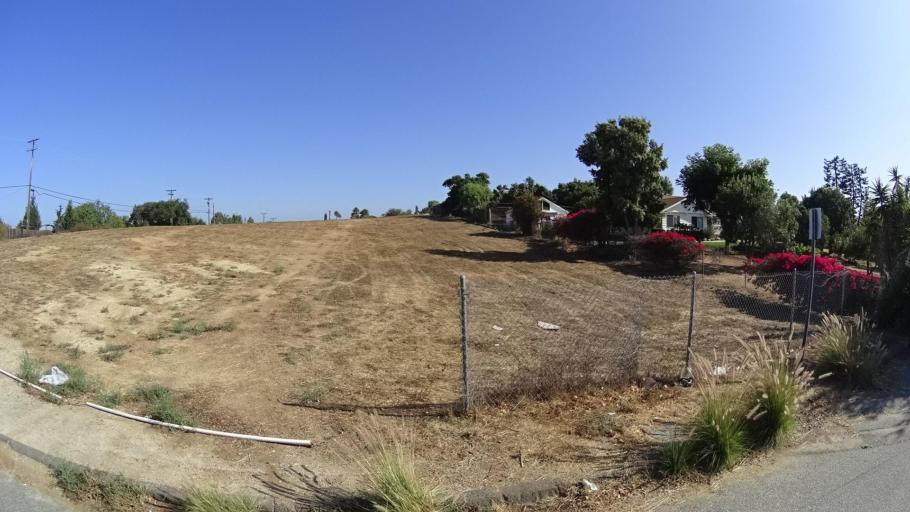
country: US
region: California
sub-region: San Diego County
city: Fallbrook
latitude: 33.3766
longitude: -117.2273
